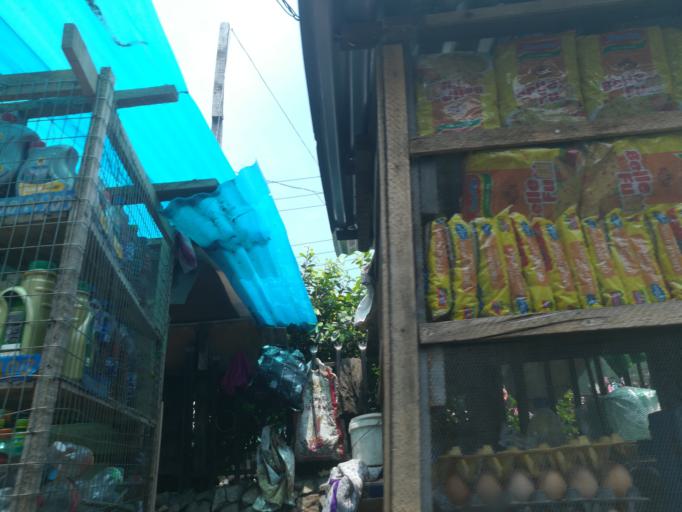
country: NG
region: Lagos
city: Lagos
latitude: 6.4535
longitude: 3.3984
